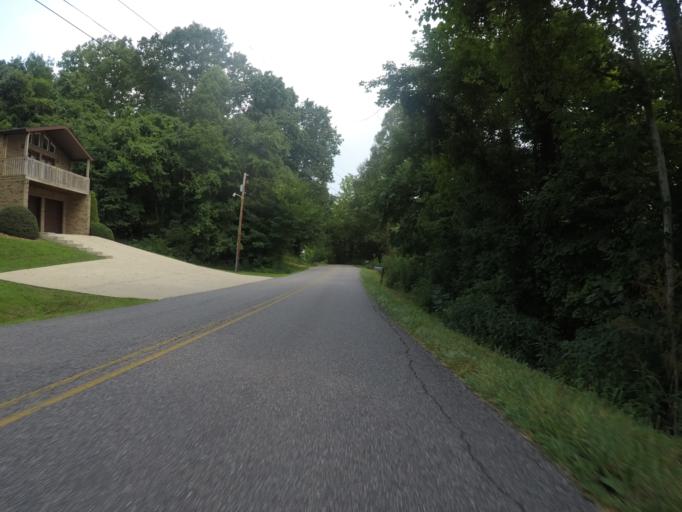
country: US
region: Kentucky
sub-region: Boyd County
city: Meads
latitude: 38.4219
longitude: -82.7076
